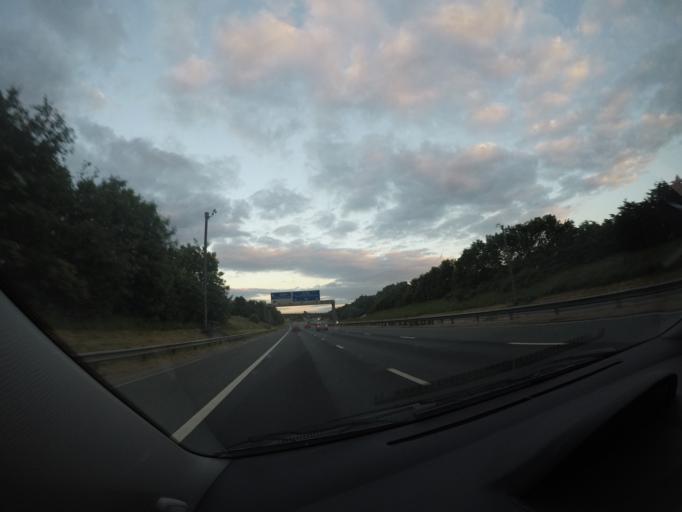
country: GB
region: England
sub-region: North Yorkshire
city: Boroughbridge
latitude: 54.0873
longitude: -1.4016
